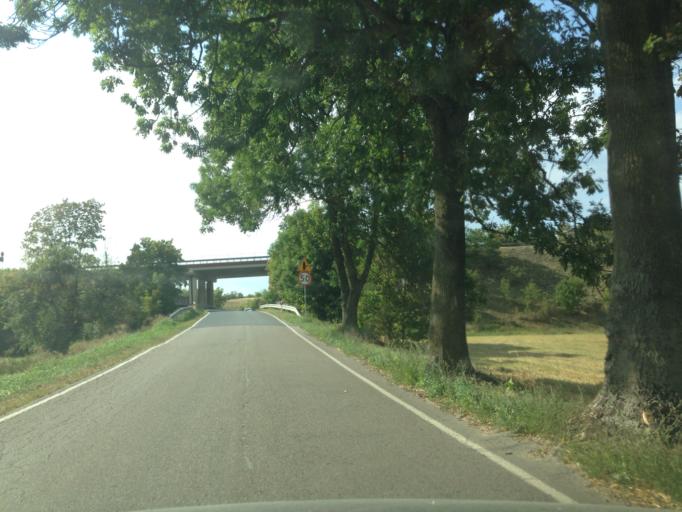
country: PL
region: Kujawsko-Pomorskie
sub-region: Powiat swiecki
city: Bukowiec
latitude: 53.3547
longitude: 18.3070
